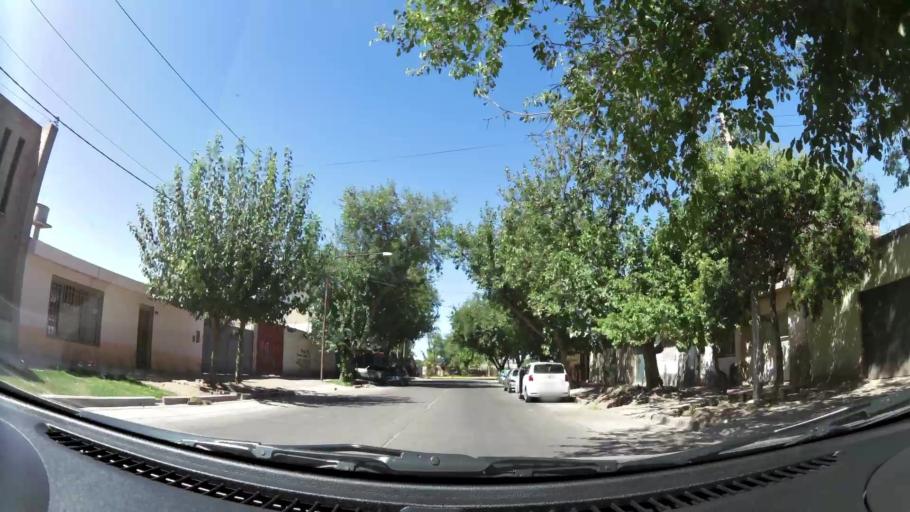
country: AR
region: Mendoza
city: Mendoza
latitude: -32.8854
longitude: -68.8132
